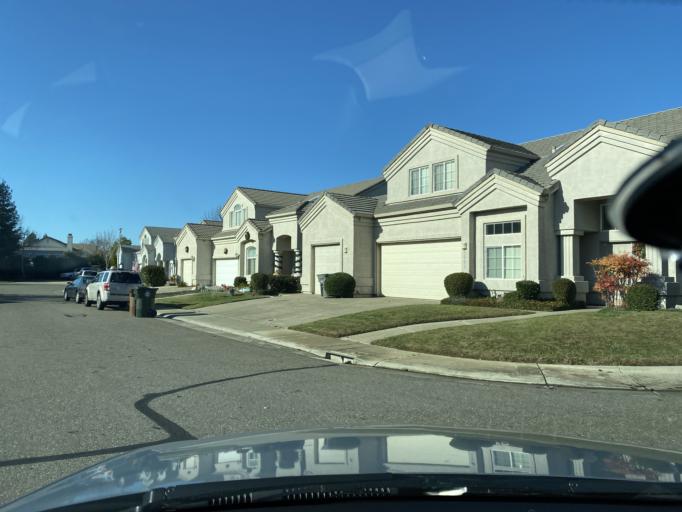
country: US
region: California
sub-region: Sacramento County
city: Elk Grove
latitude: 38.4364
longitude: -121.3815
